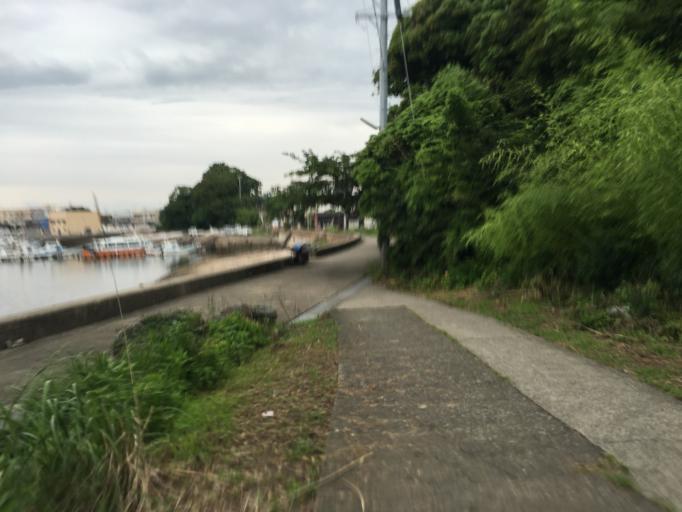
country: JP
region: Aichi
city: Ishiki
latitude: 34.7190
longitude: 137.0504
